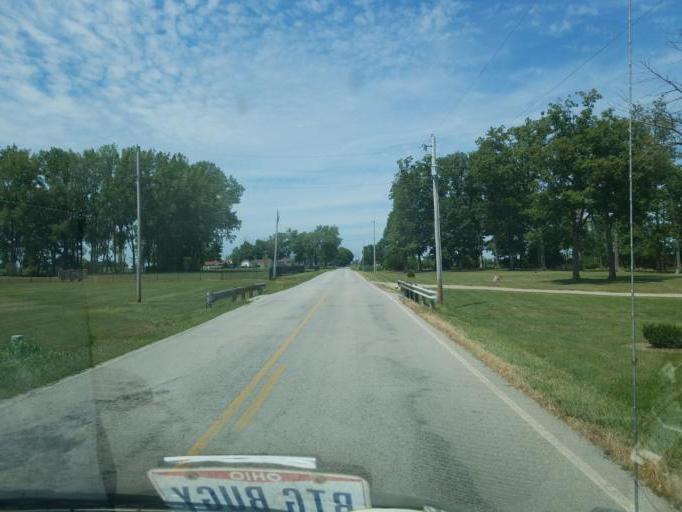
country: US
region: Ohio
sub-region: Madison County
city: West Jefferson
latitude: 39.9858
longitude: -83.2817
